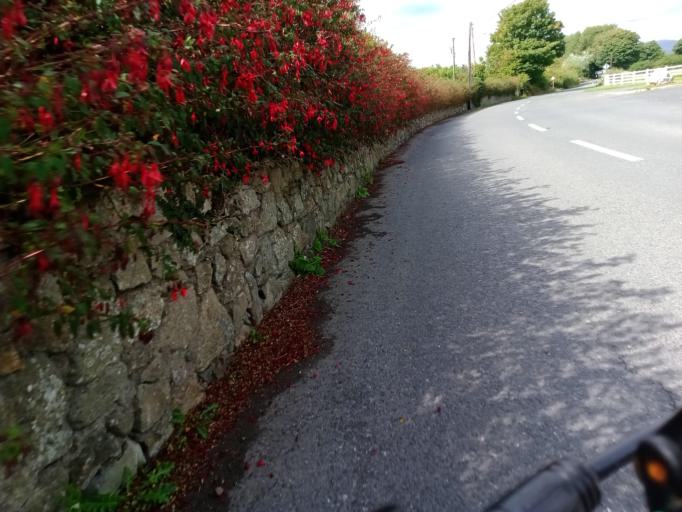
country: IE
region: Munster
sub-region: Waterford
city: Dungarvan
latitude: 52.1362
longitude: -7.4687
